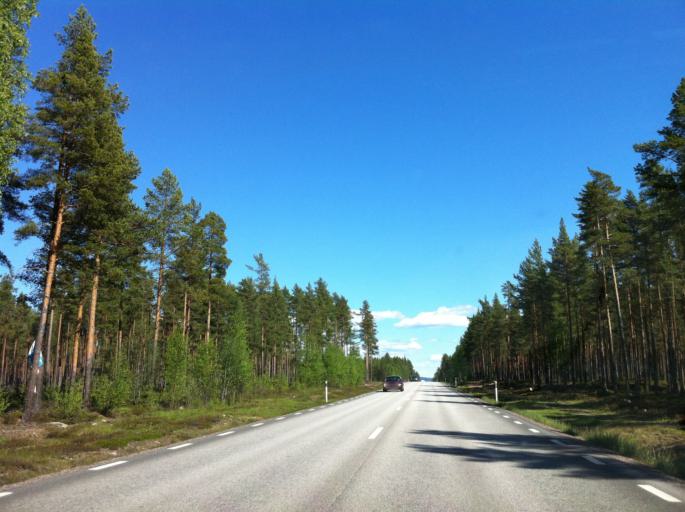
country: SE
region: Dalarna
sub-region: Rattviks Kommun
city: Vikarbyn
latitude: 60.9107
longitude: 14.9079
